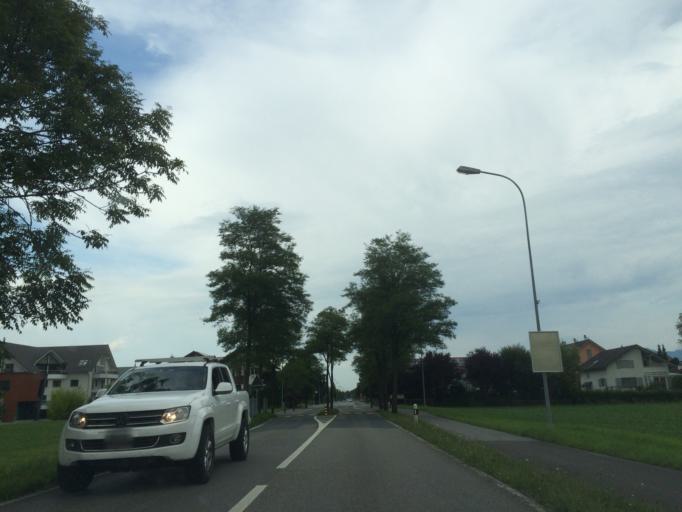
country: LI
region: Ruggell
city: Ruggell
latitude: 47.2345
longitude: 9.5187
